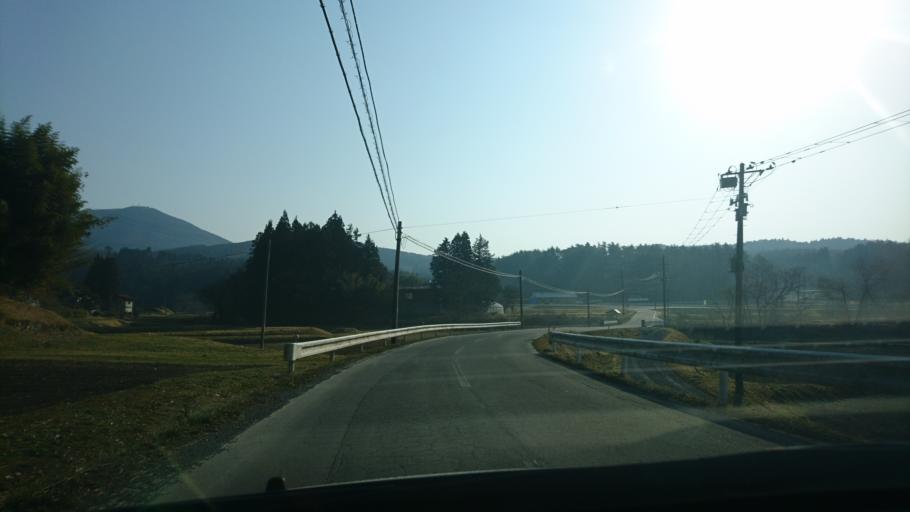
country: JP
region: Iwate
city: Ichinoseki
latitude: 38.9527
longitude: 141.4096
